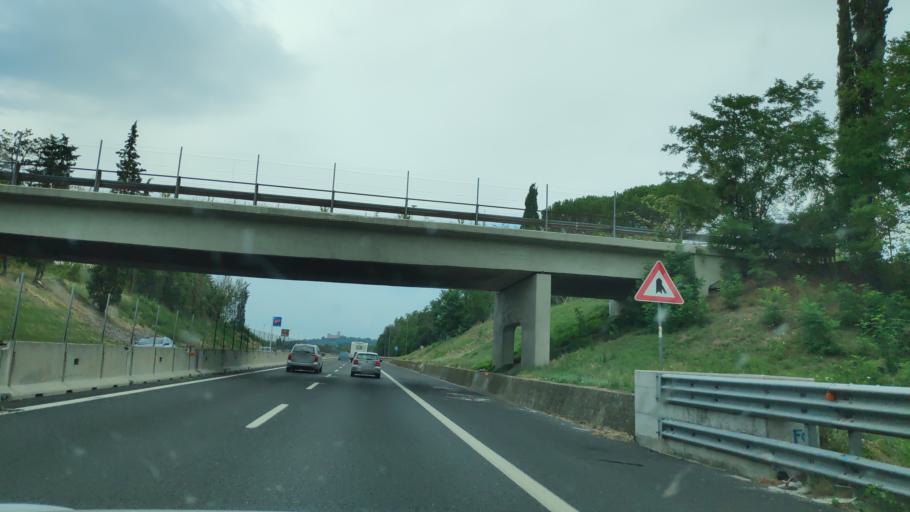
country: IT
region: Tuscany
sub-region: Province of Florence
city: Incisa in Val d'Arno
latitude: 43.6506
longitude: 11.4657
